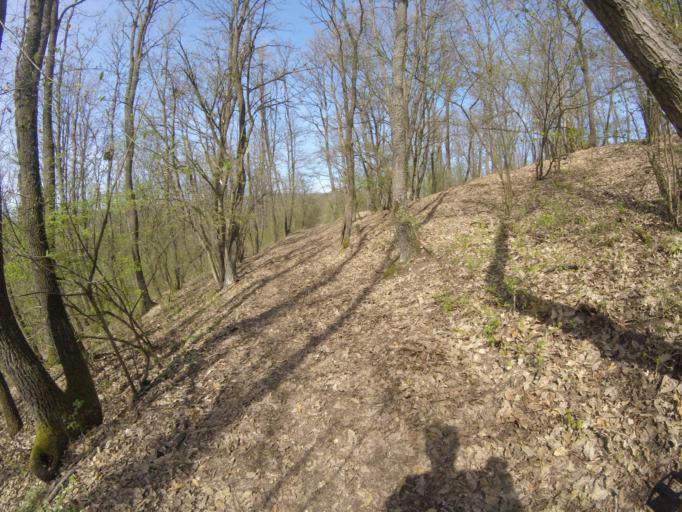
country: HU
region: Borsod-Abauj-Zemplen
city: Szendro
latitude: 48.4250
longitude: 20.7549
